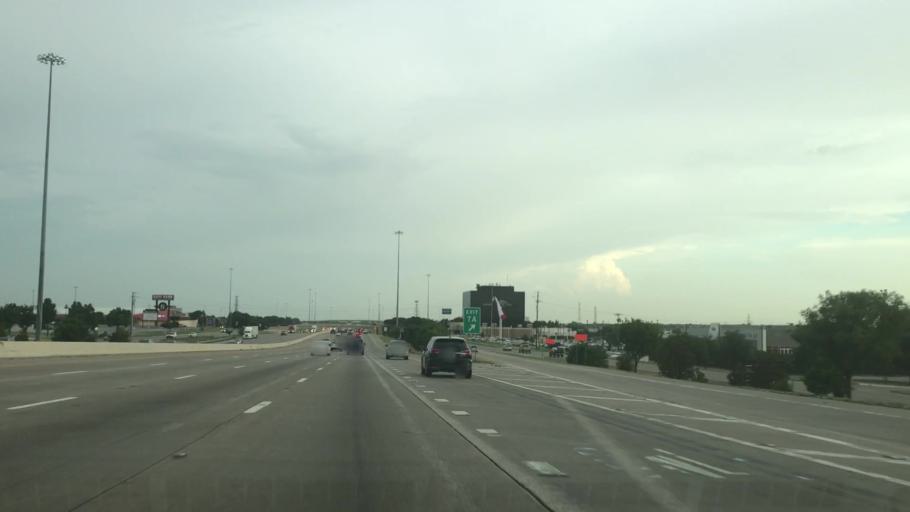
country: US
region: Texas
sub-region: Dallas County
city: Mesquite
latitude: 32.8087
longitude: -96.6277
